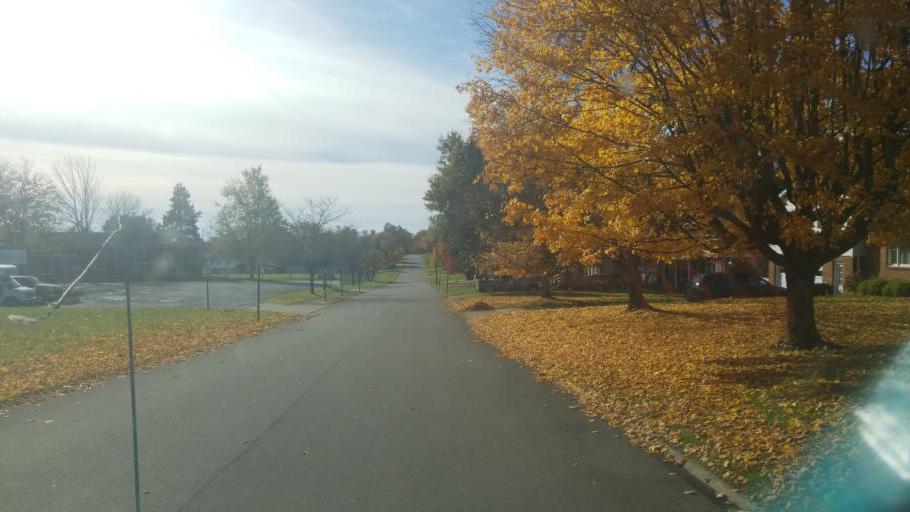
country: US
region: Ohio
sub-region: Richland County
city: Mansfield
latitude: 40.7320
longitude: -82.5290
